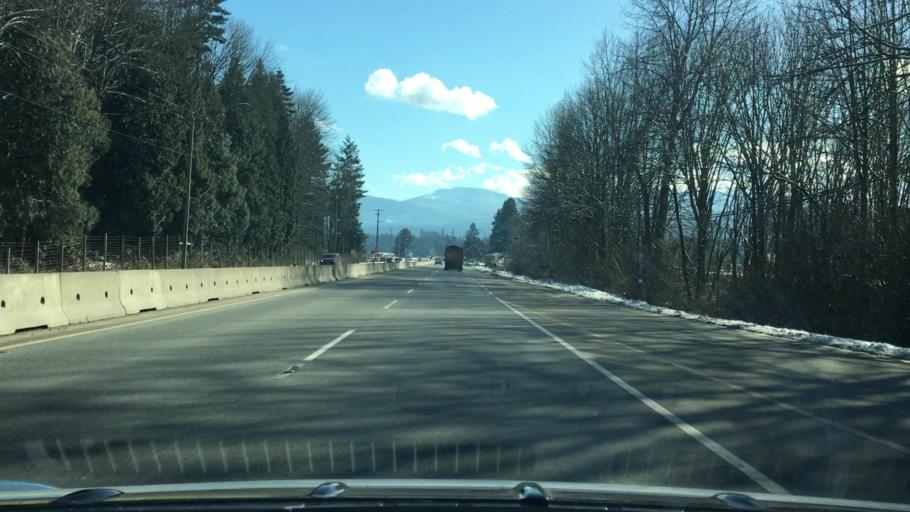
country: CA
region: British Columbia
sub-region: Cowichan Valley Regional District
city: Ladysmith
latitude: 49.0595
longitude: -123.8778
